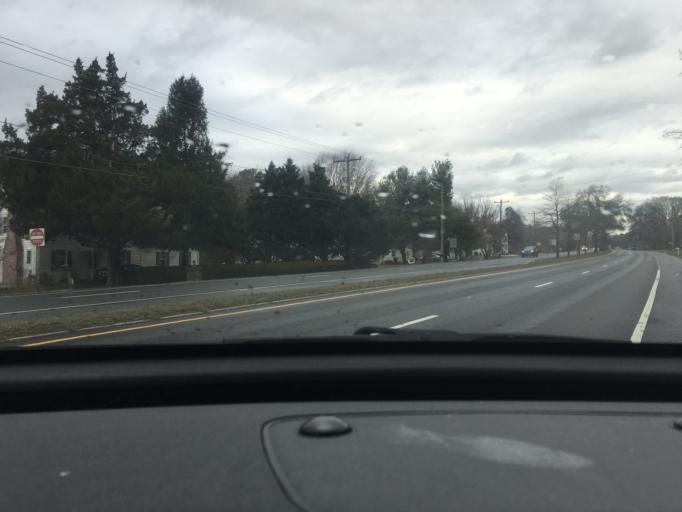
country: US
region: Maryland
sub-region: Wicomico County
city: Salisbury
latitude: 38.3796
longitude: -75.6185
